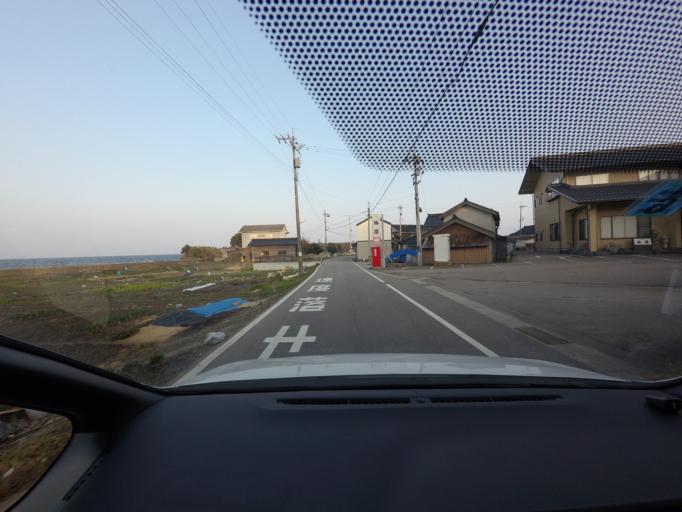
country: JP
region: Ishikawa
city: Nanao
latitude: 37.1569
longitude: 137.0474
